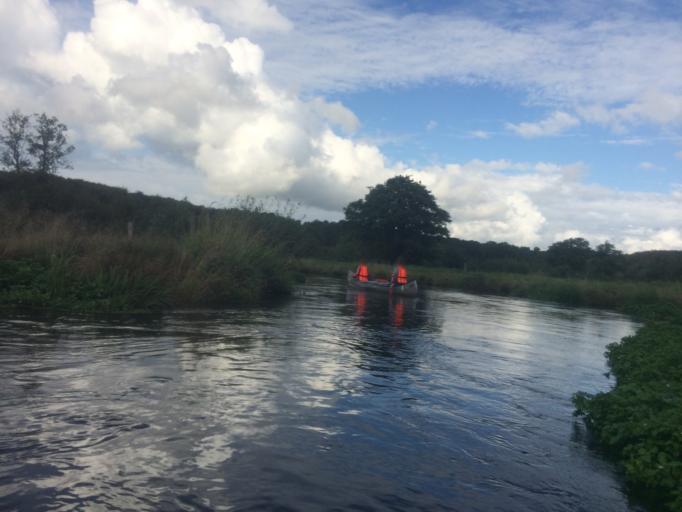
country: DK
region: South Denmark
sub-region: Vejle Kommune
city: Egtved
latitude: 55.6606
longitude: 9.3161
